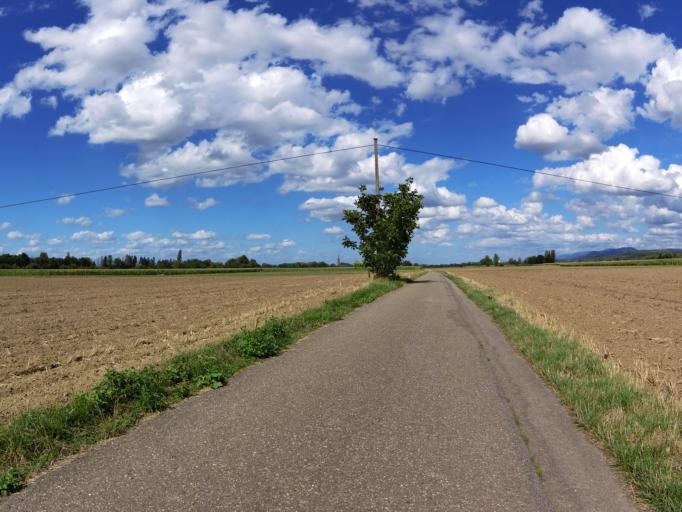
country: DE
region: Baden-Wuerttemberg
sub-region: Freiburg Region
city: Lahr
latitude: 48.3622
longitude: 7.8447
